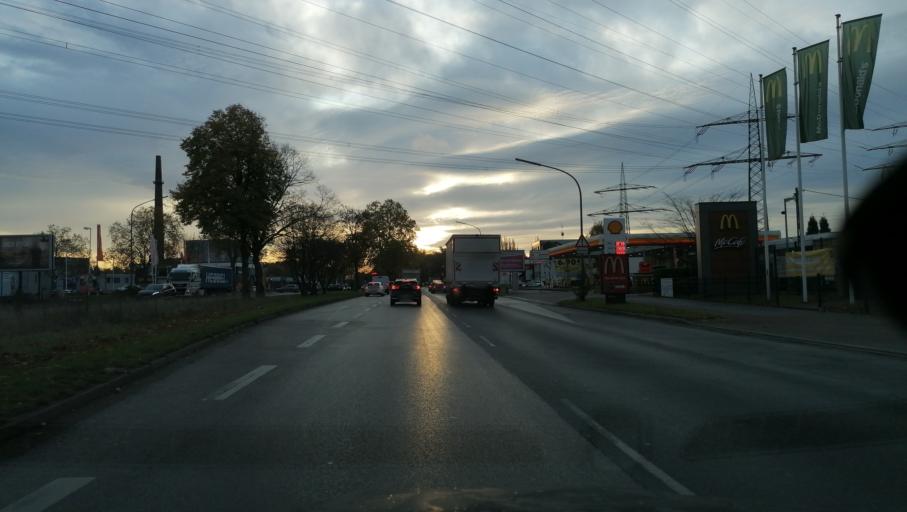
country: DE
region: North Rhine-Westphalia
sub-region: Regierungsbezirk Munster
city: Gelsenkirchen
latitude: 51.5219
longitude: 7.0736
